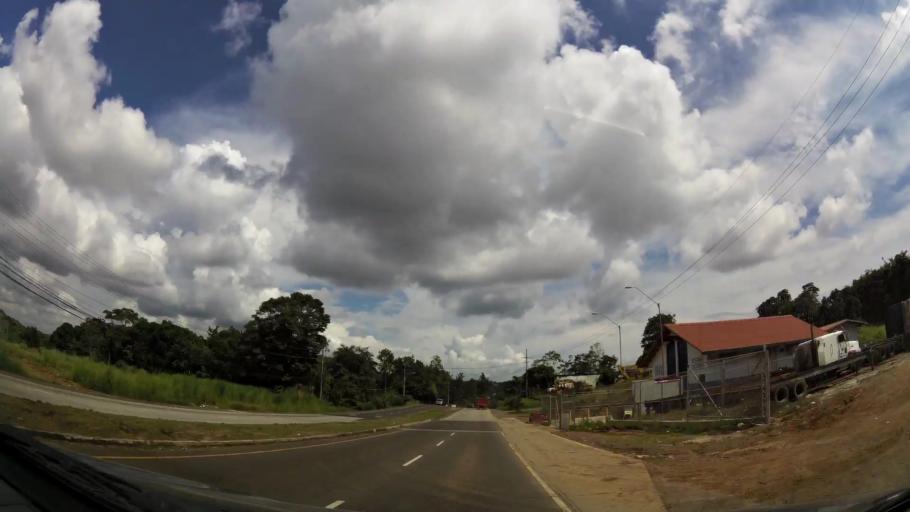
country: PA
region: Panama
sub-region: Distrito Arraijan
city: Arraijan
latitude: 8.9470
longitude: -79.6736
